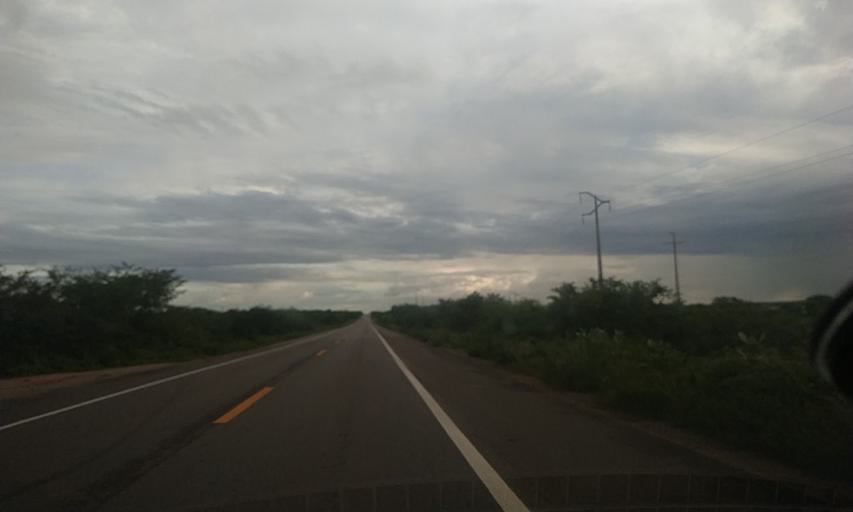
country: BR
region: Rio Grande do Norte
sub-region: Mossoro
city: Mossoro
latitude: -5.1394
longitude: -37.2124
